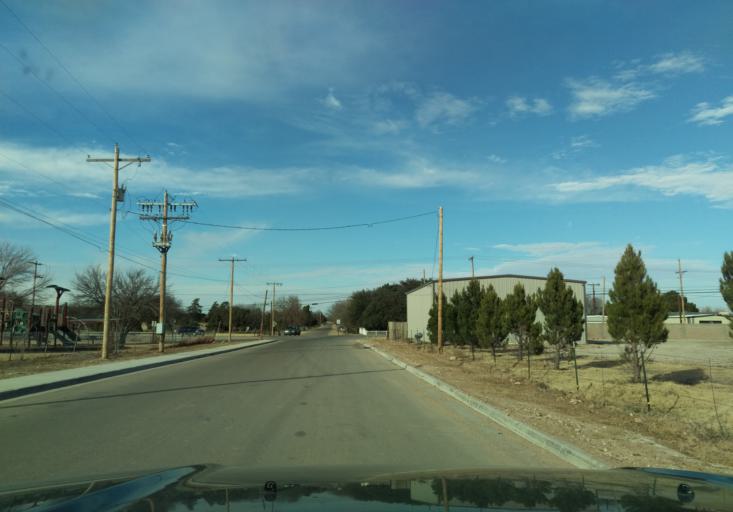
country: US
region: New Mexico
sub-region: Eddy County
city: La Huerta
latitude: 32.4492
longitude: -104.2376
